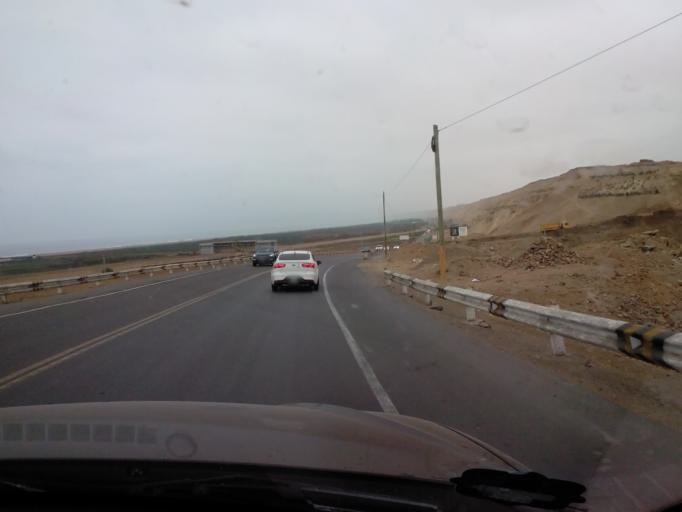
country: PE
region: Ica
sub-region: Provincia de Chincha
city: Sunampe
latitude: -13.4131
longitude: -76.1889
